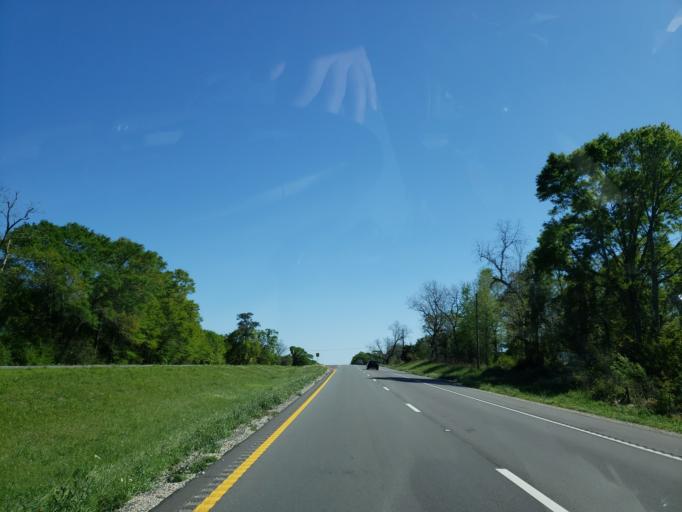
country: US
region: Mississippi
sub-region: Stone County
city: Wiggins
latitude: 30.8988
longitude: -89.1678
